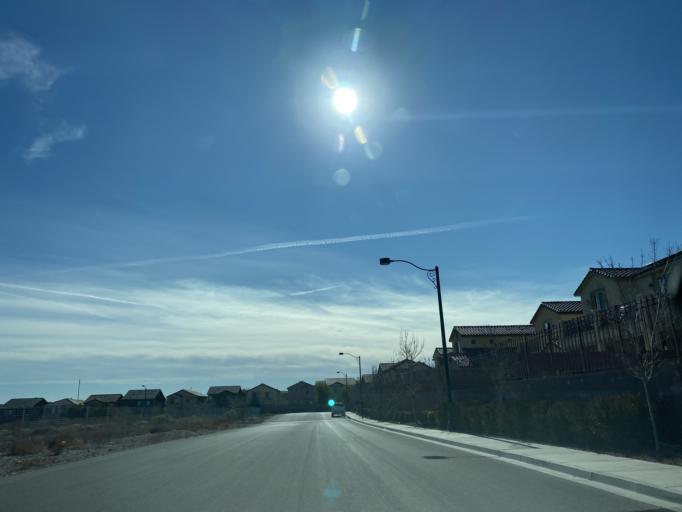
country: US
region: Nevada
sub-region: Clark County
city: Summerlin South
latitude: 36.2967
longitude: -115.3265
